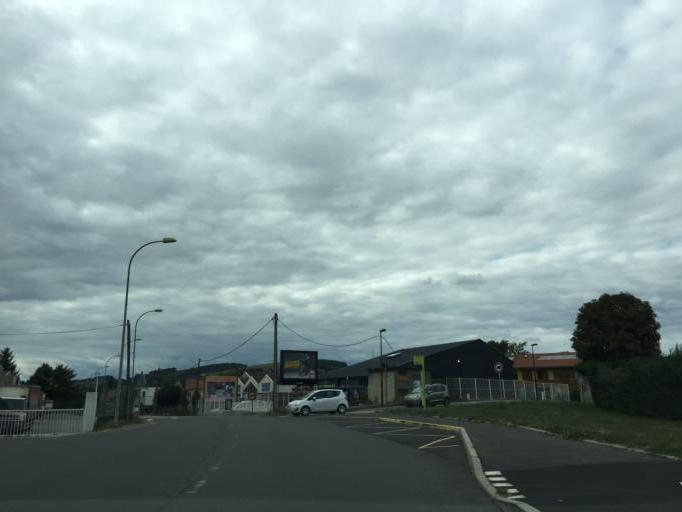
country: FR
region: Rhone-Alpes
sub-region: Departement de la Loire
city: Sorbiers
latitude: 45.4803
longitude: 4.4522
